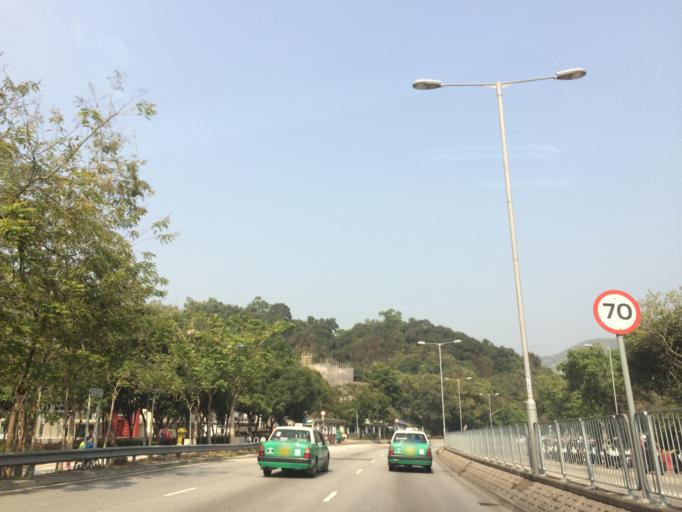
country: HK
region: Tai Po
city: Tai Po
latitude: 22.4571
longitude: 114.1775
